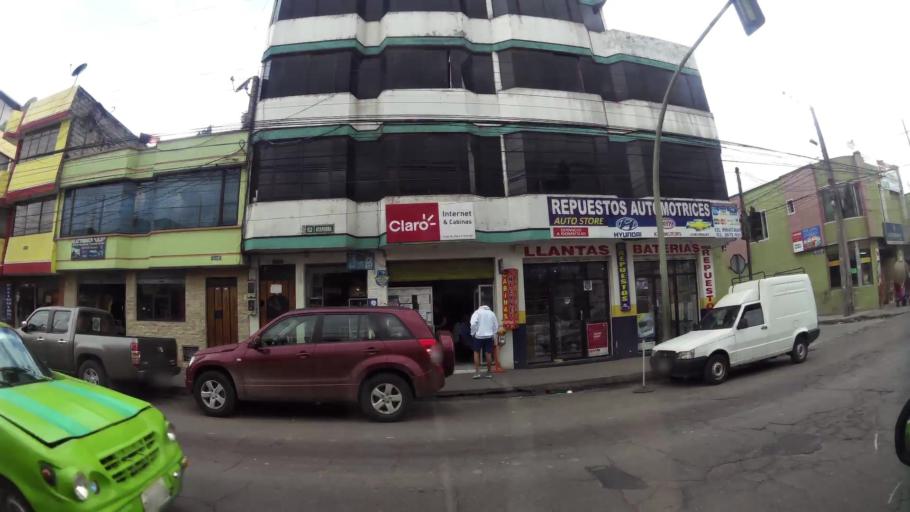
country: EC
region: Pichincha
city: Quito
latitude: -0.2754
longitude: -78.5357
